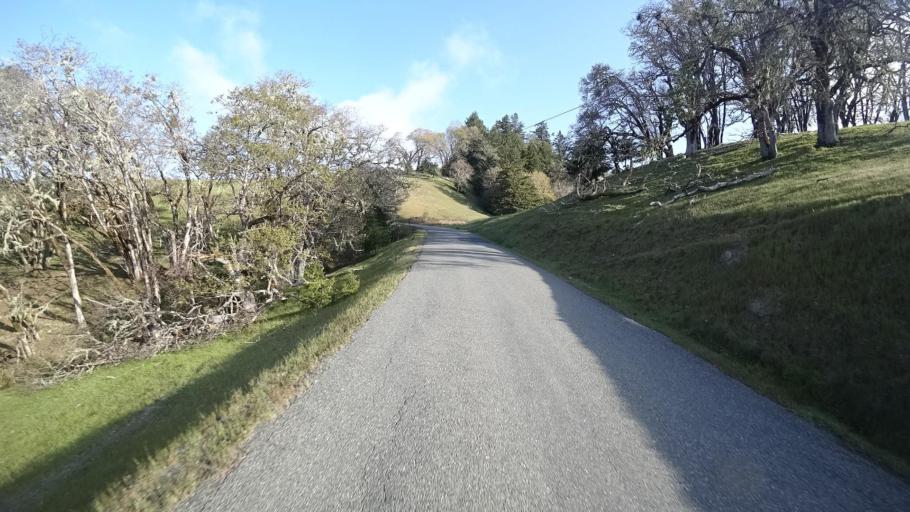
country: US
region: California
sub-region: Humboldt County
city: Blue Lake
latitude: 40.7174
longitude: -123.9404
